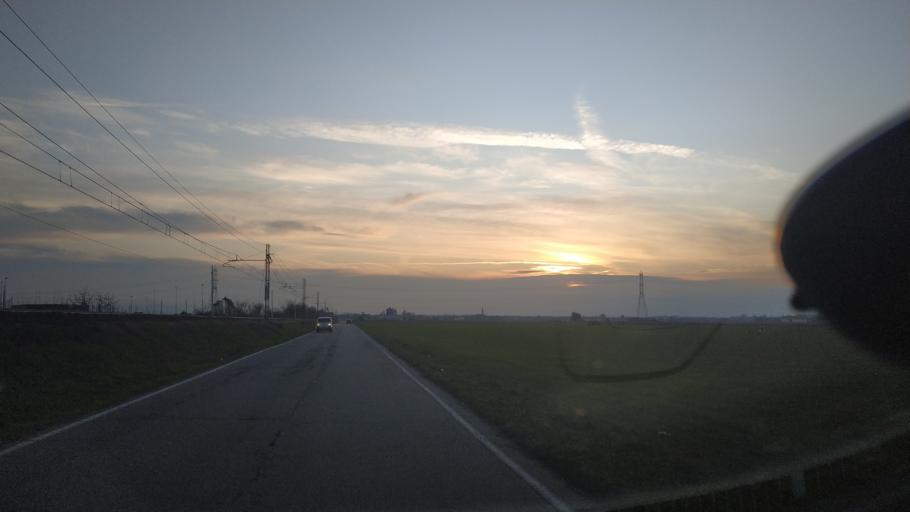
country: IT
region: Piedmont
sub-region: Provincia di Torino
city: Caluso
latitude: 45.2908
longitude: 7.8899
